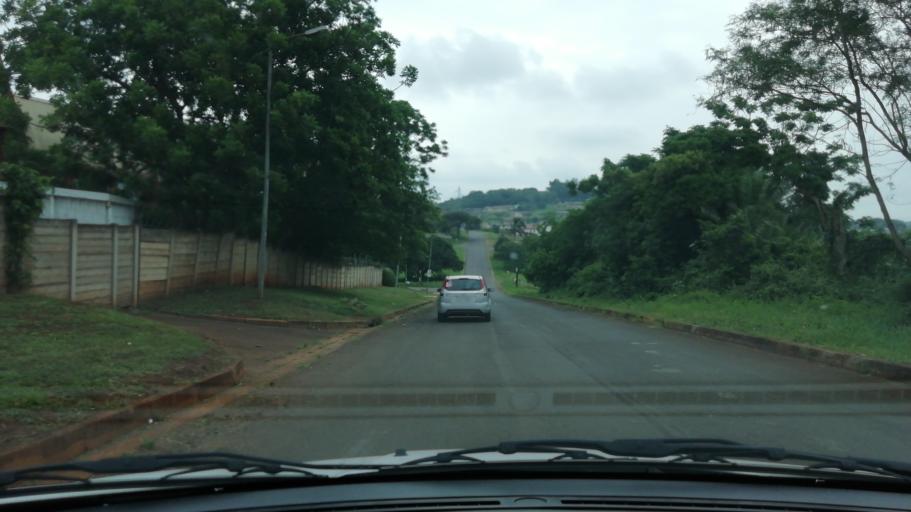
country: ZA
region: KwaZulu-Natal
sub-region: uThungulu District Municipality
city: Empangeni
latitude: -28.7384
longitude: 31.8868
